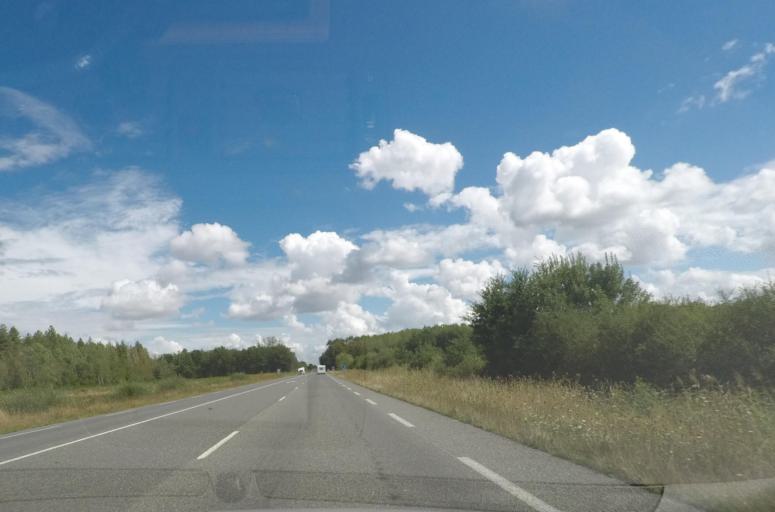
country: FR
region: Pays de la Loire
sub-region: Departement de la Sarthe
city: Parigne-le-Polin
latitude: 47.8638
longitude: 0.1115
